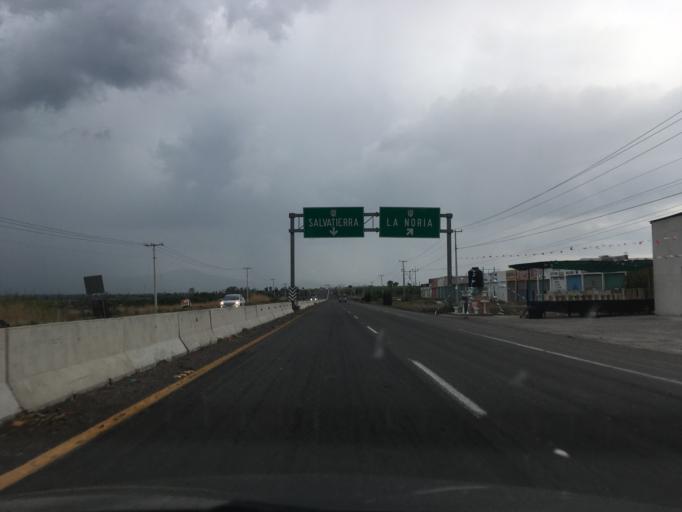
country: MX
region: Guanajuato
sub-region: Tarimoro
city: San Juan Bautista Cacalote
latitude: 20.3526
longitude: -100.8030
